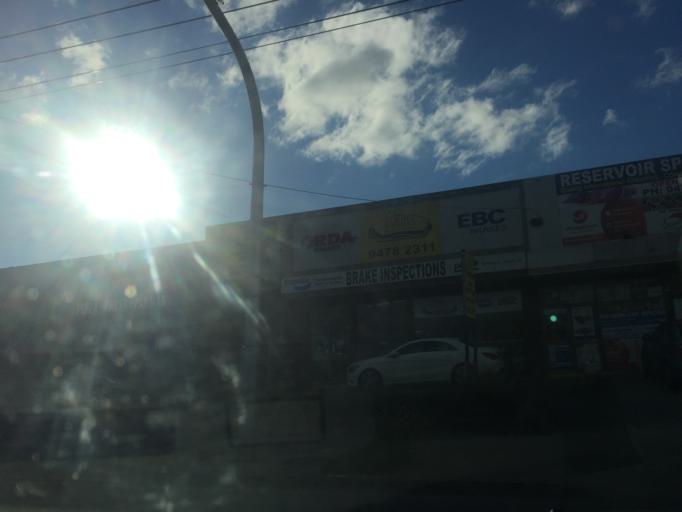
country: AU
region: Victoria
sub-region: Darebin
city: Preston
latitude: -37.7302
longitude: 145.0158
